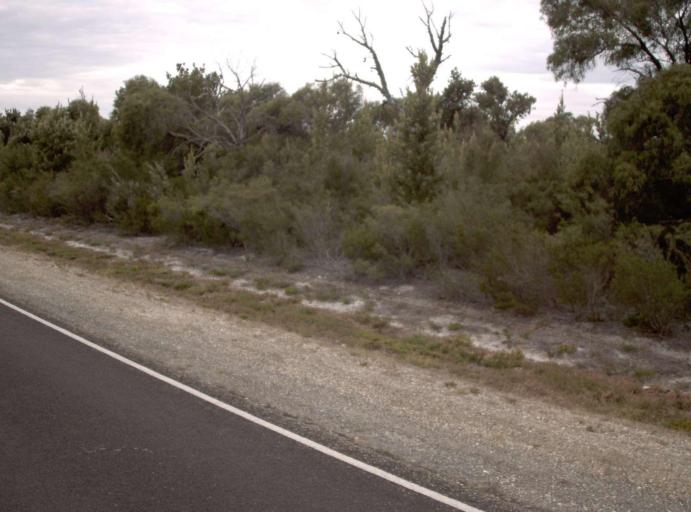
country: AU
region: Victoria
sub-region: Wellington
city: Sale
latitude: -38.1953
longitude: 147.3623
